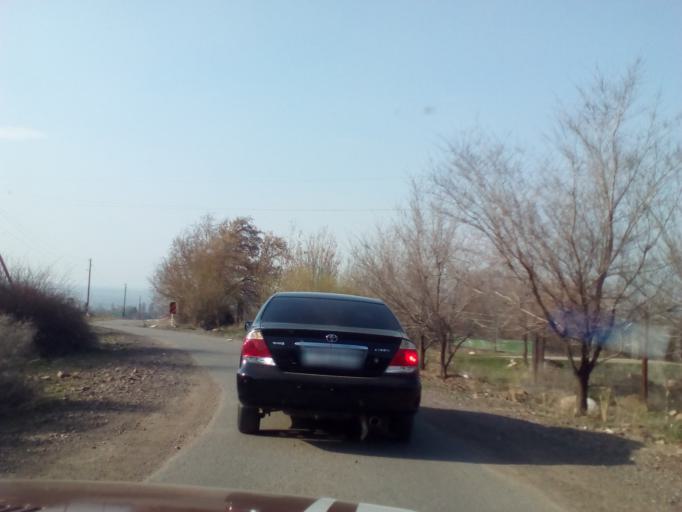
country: KZ
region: Almaty Oblysy
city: Burunday
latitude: 43.1523
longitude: 76.5731
